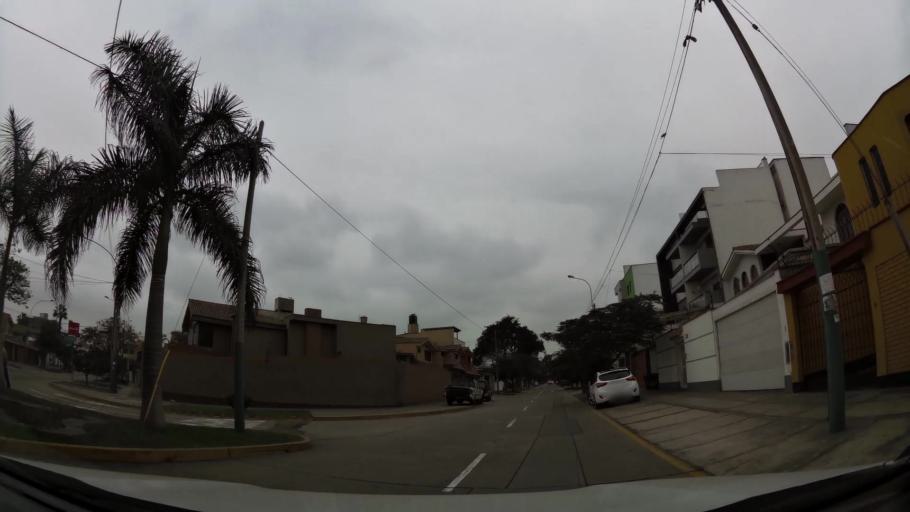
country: PE
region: Lima
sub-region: Lima
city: San Luis
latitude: -12.0985
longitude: -77.0001
